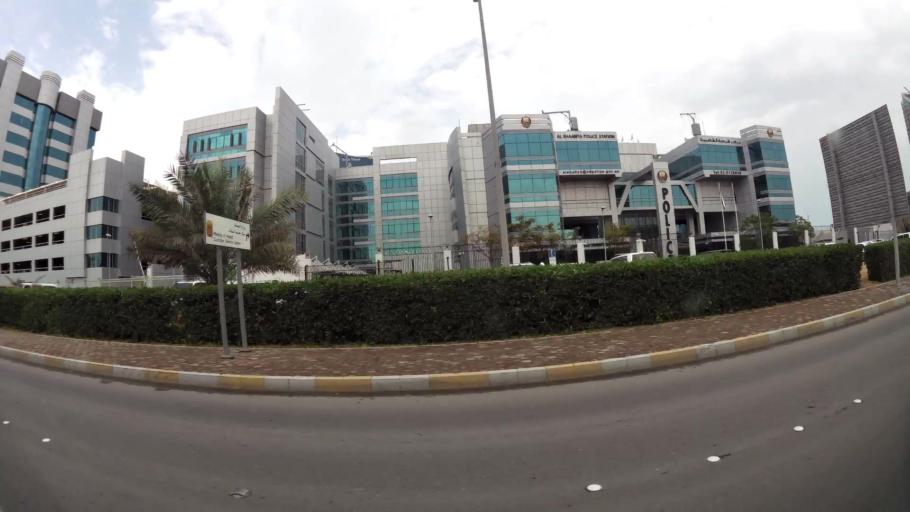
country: AE
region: Abu Dhabi
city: Abu Dhabi
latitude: 24.4525
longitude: 54.3985
